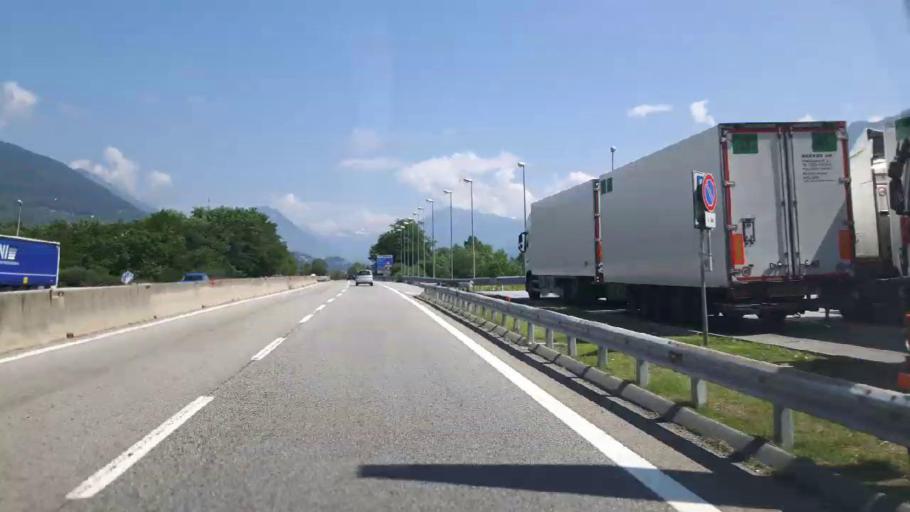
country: IT
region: Piedmont
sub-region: Provincia Verbano-Cusio-Ossola
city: Villadossola
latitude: 46.0646
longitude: 8.2765
